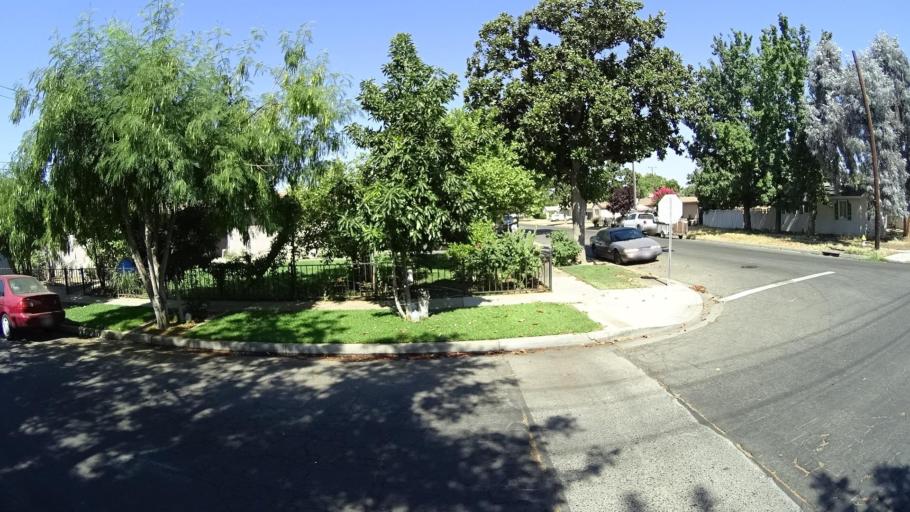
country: US
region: California
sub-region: Fresno County
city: Fresno
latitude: 36.7976
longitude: -119.7769
